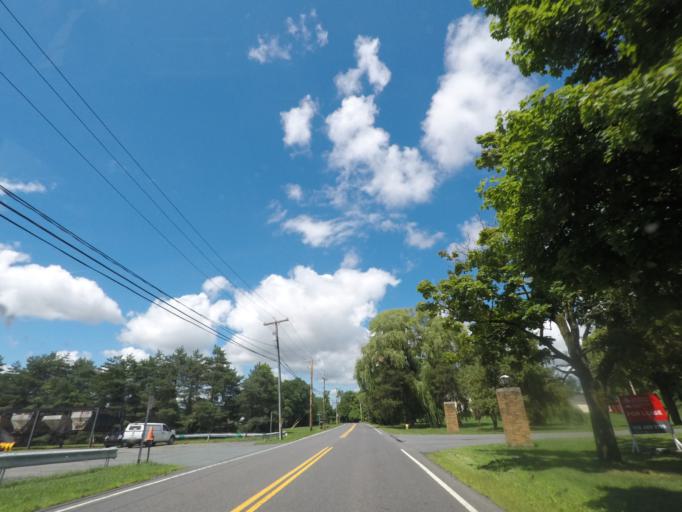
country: US
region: New York
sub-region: Rensselaer County
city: Wynantskill
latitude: 42.6874
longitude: -73.6817
